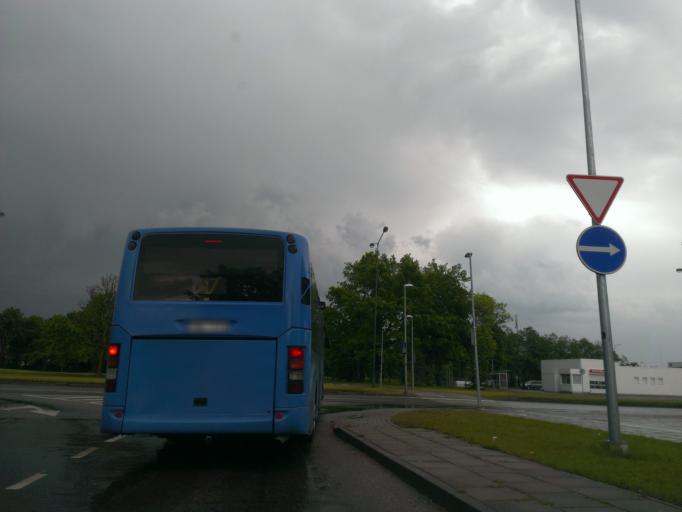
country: LT
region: Klaipedos apskritis
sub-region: Klaipeda
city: Klaipeda
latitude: 55.7544
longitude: 21.1298
